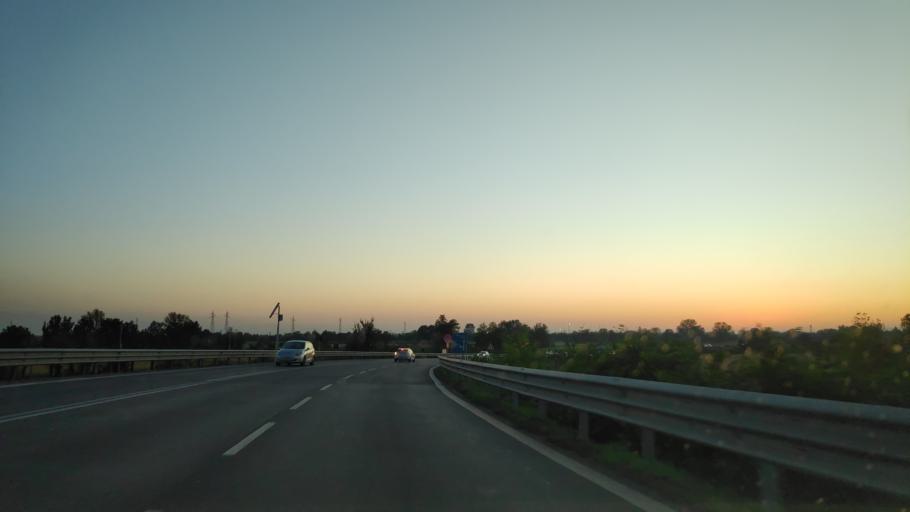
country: IT
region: Lombardy
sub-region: Citta metropolitana di Milano
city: Gaggiano
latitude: 45.4072
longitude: 9.0257
